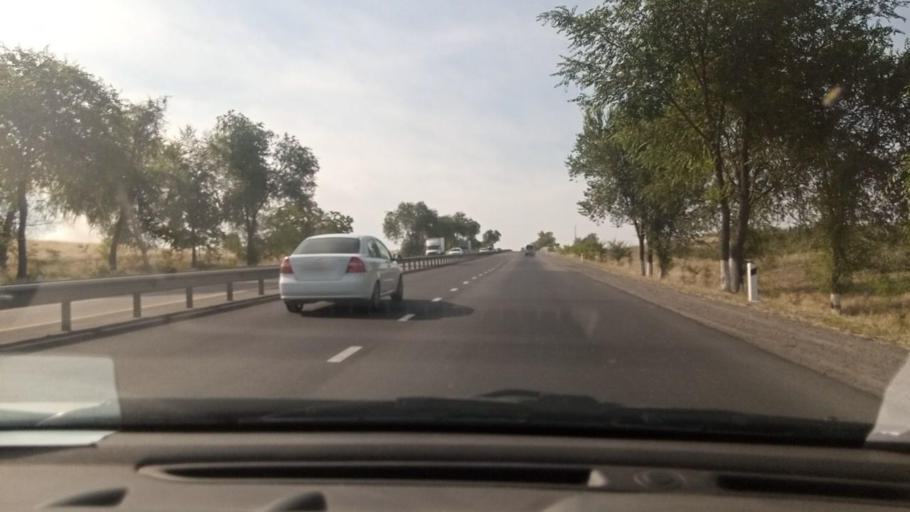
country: UZ
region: Toshkent
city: Tuytepa
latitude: 41.1118
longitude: 69.4479
